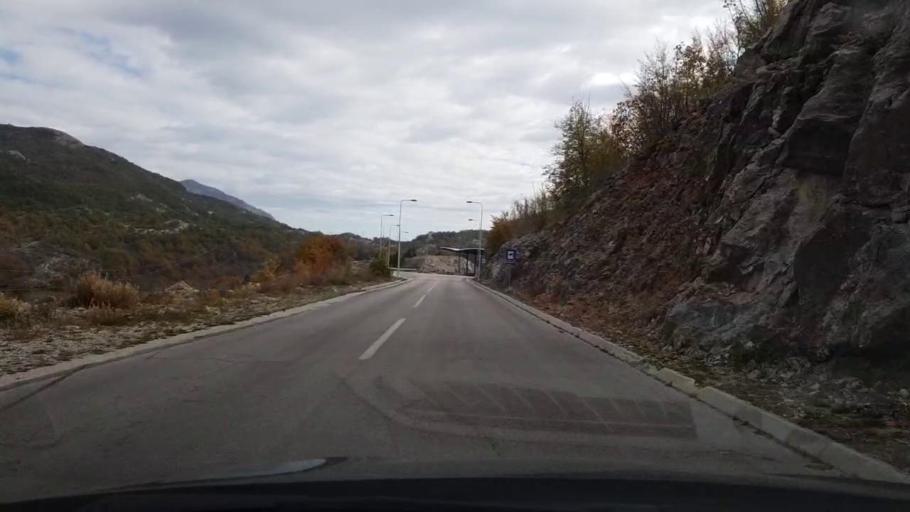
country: ME
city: Igalo
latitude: 42.5593
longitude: 18.4451
